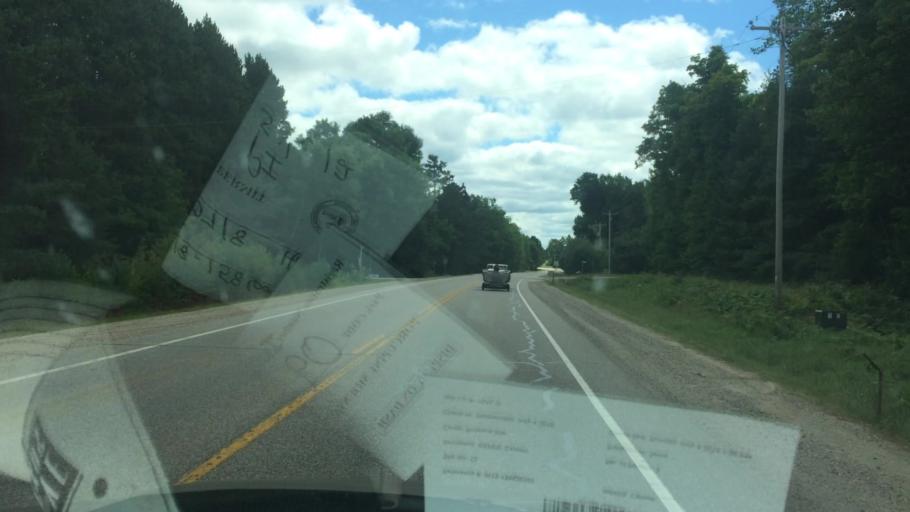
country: US
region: Wisconsin
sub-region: Vilas County
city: Eagle River
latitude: 45.8056
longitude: -89.3198
